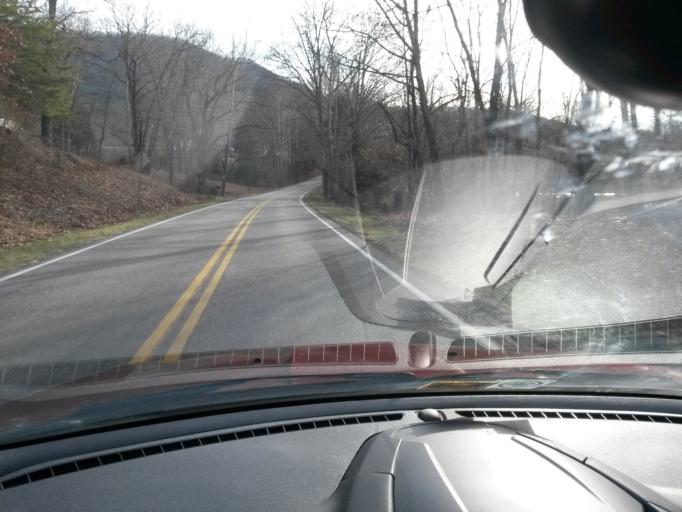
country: US
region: Virginia
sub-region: Alleghany County
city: Clifton Forge
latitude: 37.9161
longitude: -79.7254
